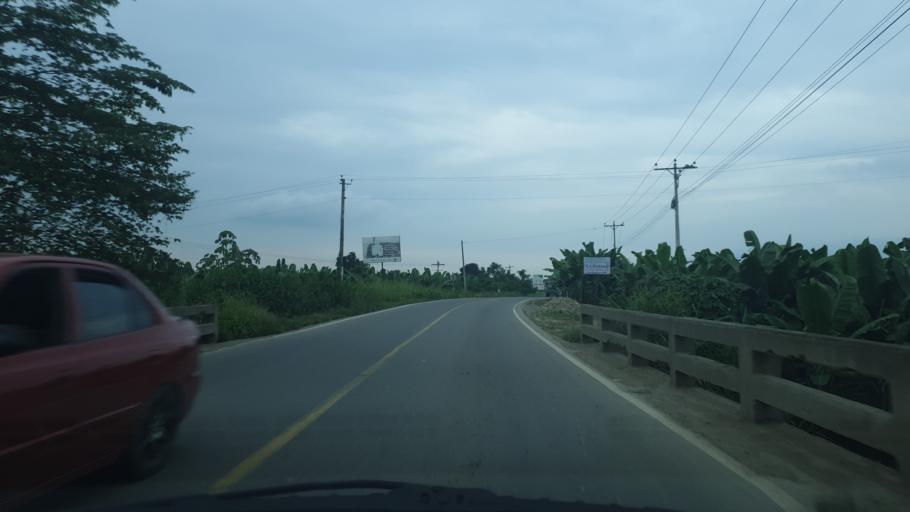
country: EC
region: El Oro
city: Pasaje
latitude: -3.3509
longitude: -79.8151
